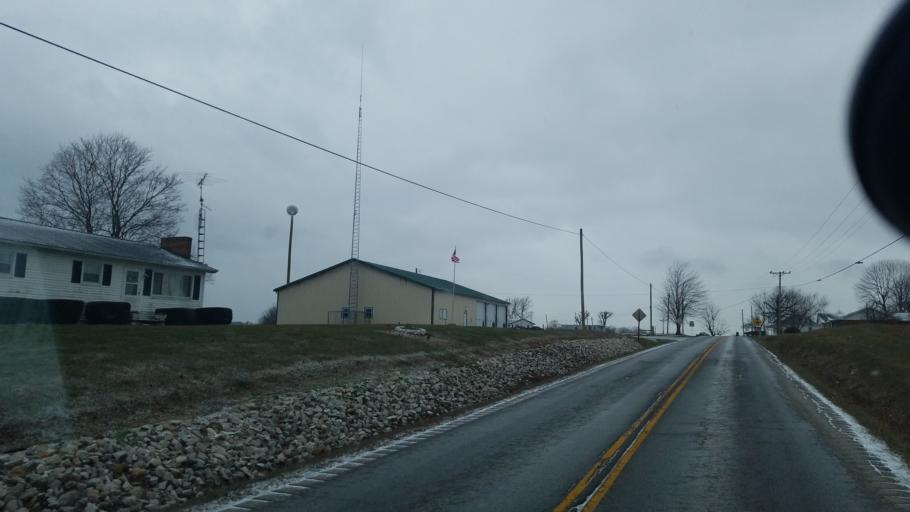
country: US
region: Kentucky
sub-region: Fleming County
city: Flemingsburg
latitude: 38.4910
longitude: -83.6227
